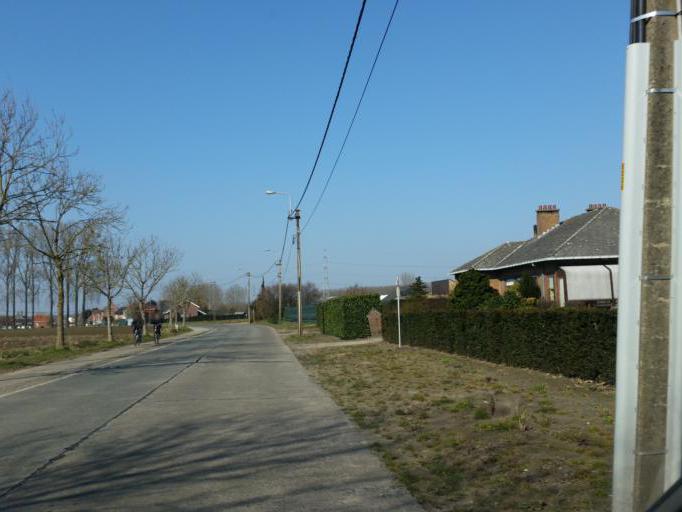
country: BE
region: Flanders
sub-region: Provincie Oost-Vlaanderen
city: Wachtebeke
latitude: 51.1310
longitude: 3.8789
